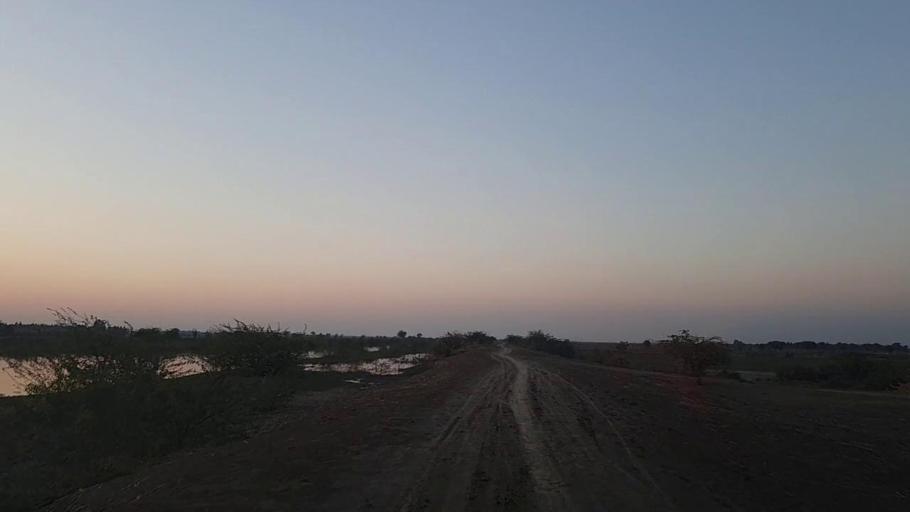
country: PK
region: Sindh
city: Tando Mittha Khan
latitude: 26.0592
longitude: 69.1664
